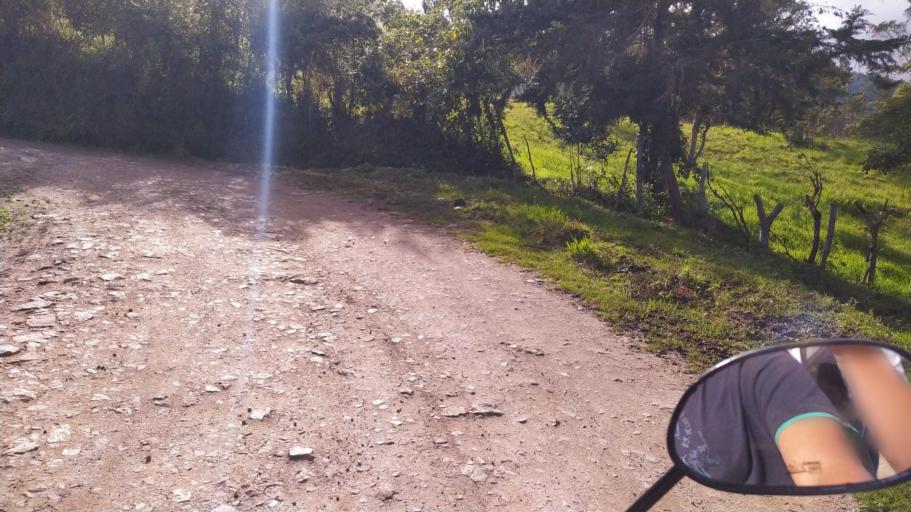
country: CO
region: Cundinamarca
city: Tenza
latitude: 5.0894
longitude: -73.4703
